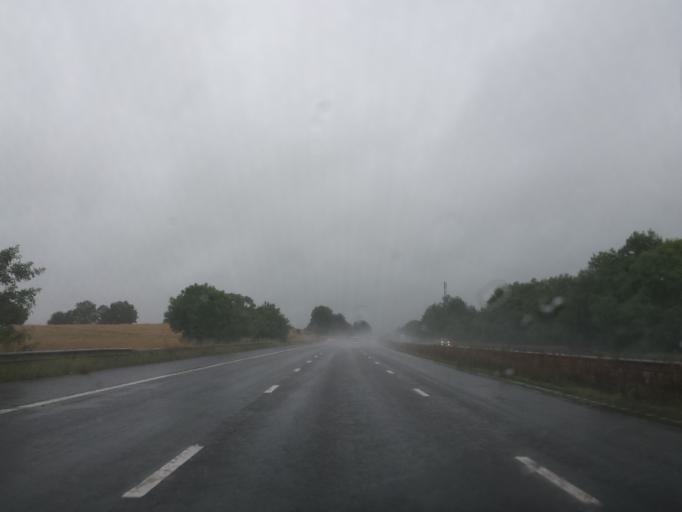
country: GB
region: England
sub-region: Warwickshire
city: Bedworth
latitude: 52.4682
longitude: -1.4070
